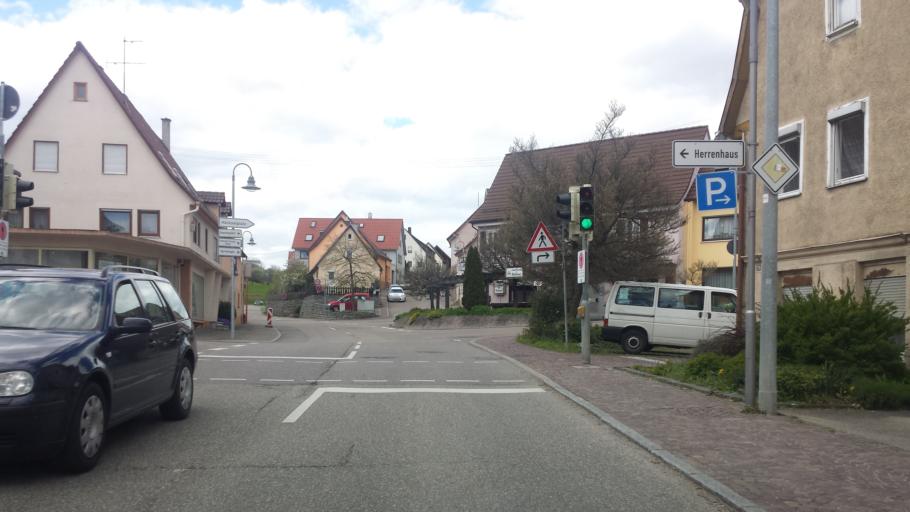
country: DE
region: Baden-Wuerttemberg
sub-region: Regierungsbezirk Stuttgart
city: Weissach
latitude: 48.8485
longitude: 8.9250
